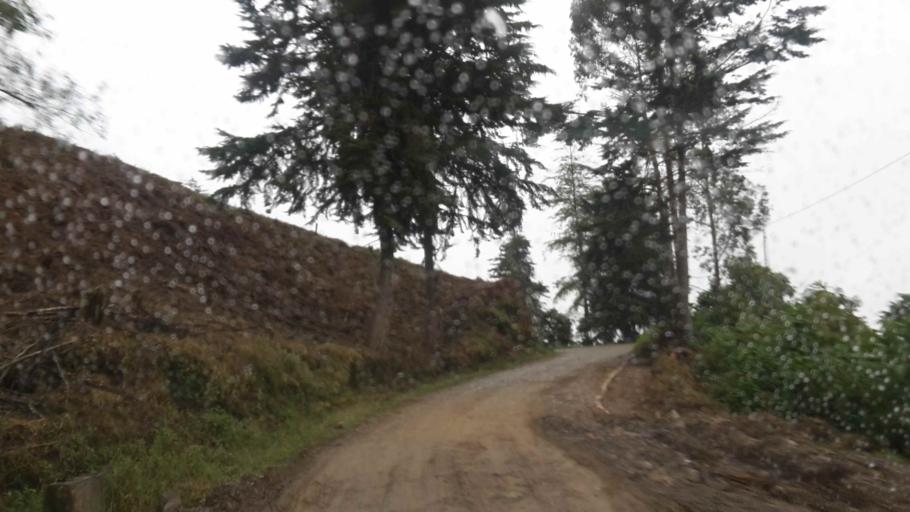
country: BO
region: Cochabamba
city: Colomi
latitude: -17.1402
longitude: -65.9190
